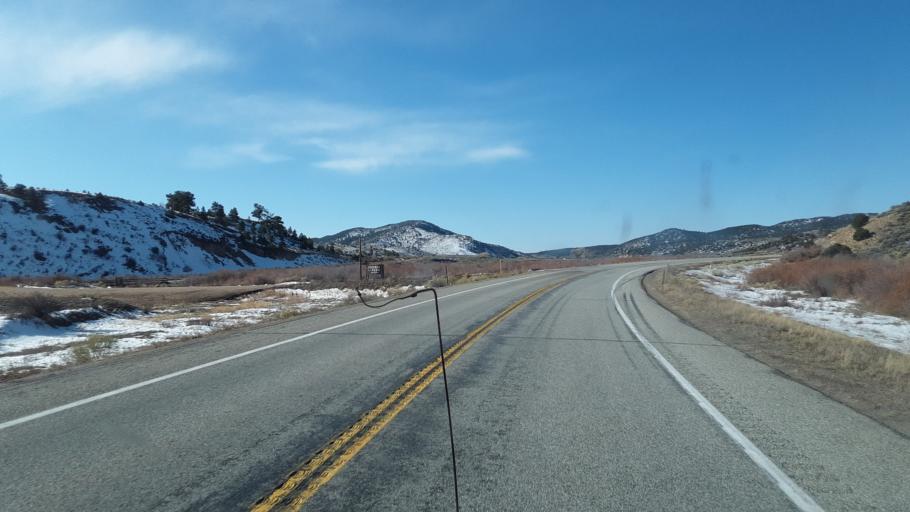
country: US
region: Colorado
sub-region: Costilla County
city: San Luis
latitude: 37.5160
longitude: -105.3022
